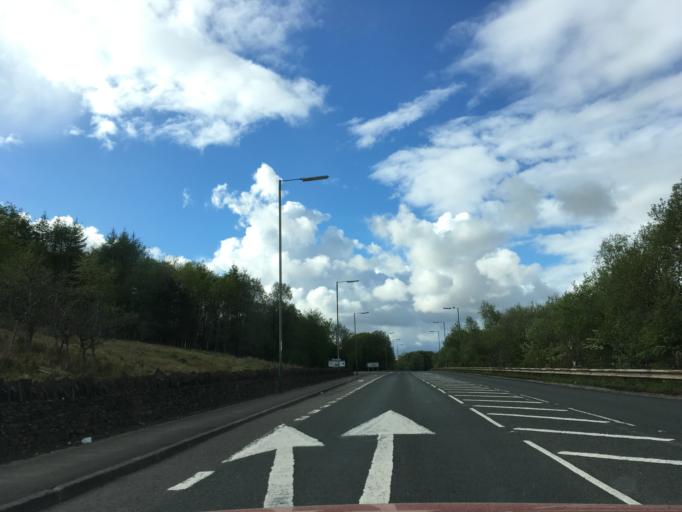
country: GB
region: Wales
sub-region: Caerphilly County Borough
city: Rhymney
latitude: 51.7539
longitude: -3.2882
